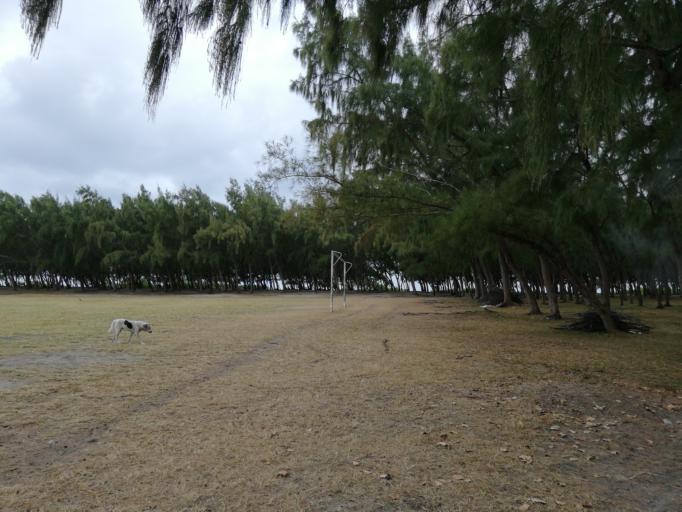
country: MU
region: Riviere du Rempart
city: Roches Noire
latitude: -20.1251
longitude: 57.7552
